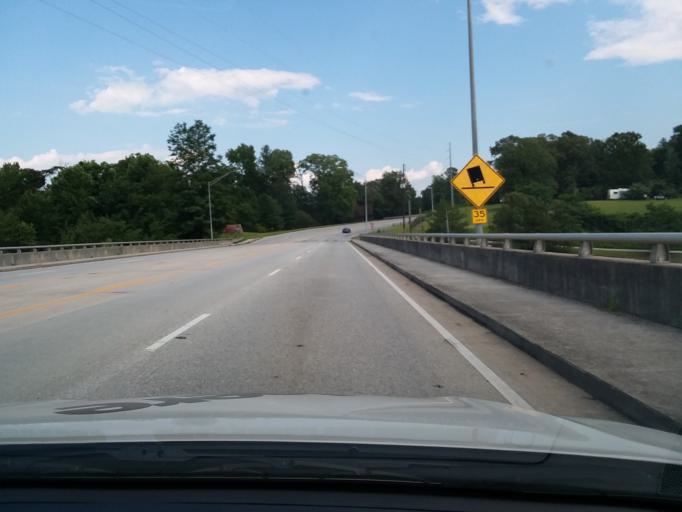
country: US
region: Georgia
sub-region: Rabun County
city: Clayton
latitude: 34.7391
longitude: -83.3957
